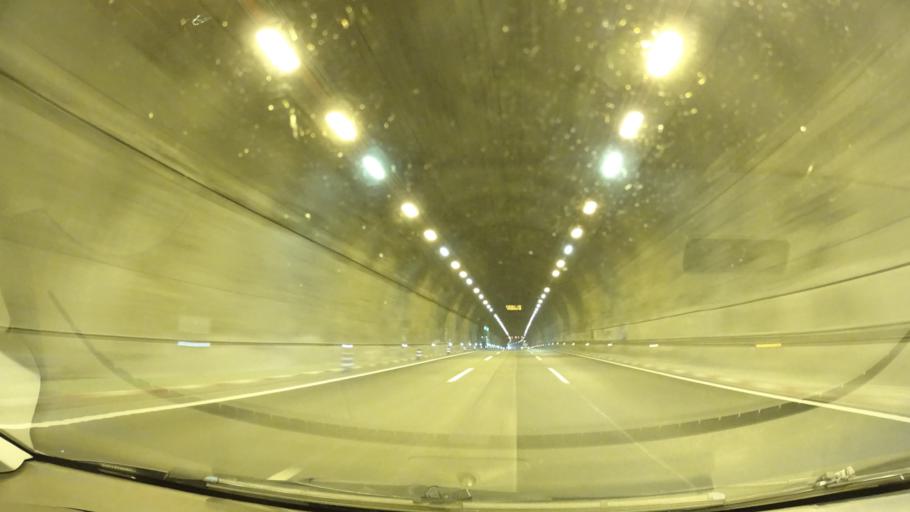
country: ES
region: Madrid
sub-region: Provincia de Madrid
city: Somosierra
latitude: 41.1329
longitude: -3.5835
